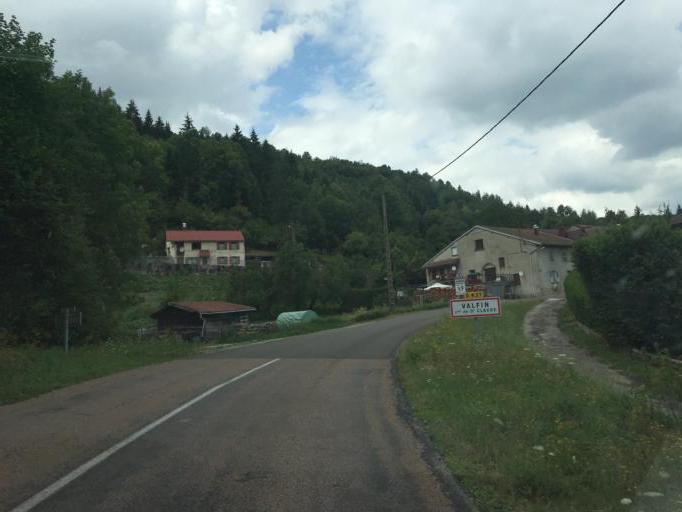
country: FR
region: Franche-Comte
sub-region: Departement du Jura
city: Valfin-les-Saint-Claude
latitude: 46.4356
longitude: 5.8541
